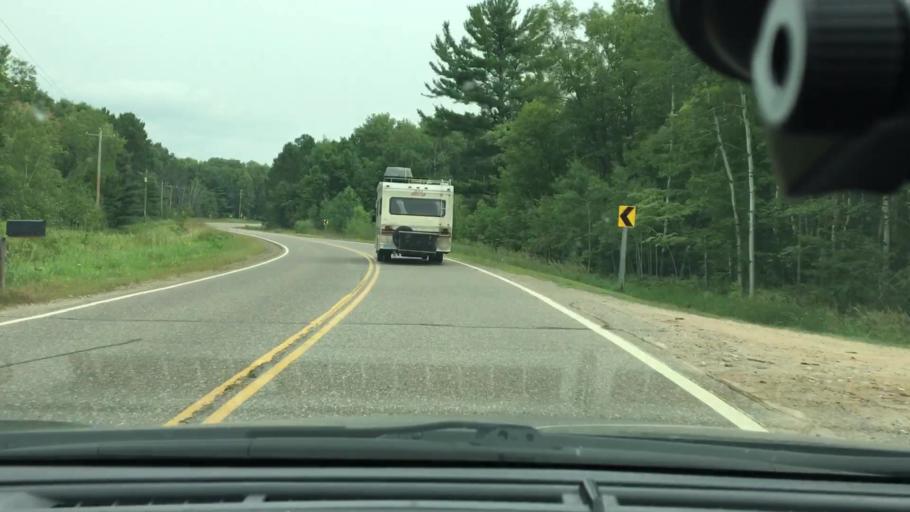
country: US
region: Minnesota
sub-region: Aitkin County
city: Aitkin
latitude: 46.4029
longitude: -93.7940
